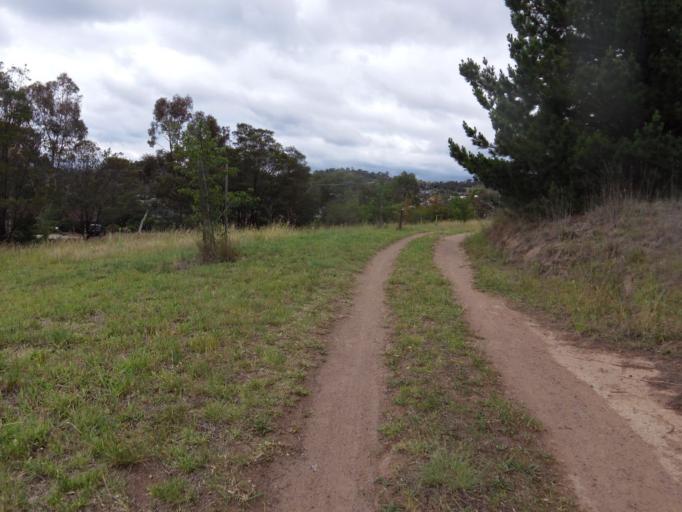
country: AU
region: Australian Capital Territory
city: Macquarie
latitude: -35.3400
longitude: 149.0275
